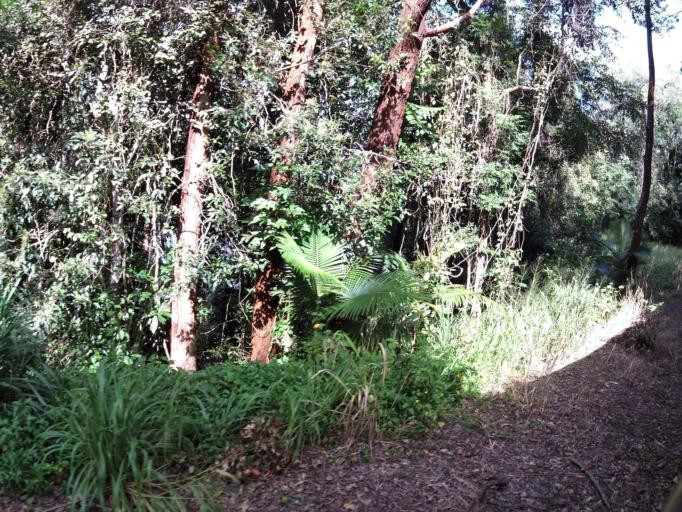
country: AU
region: Queensland
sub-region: Tablelands
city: Kuranda
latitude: -16.8276
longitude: 145.6384
